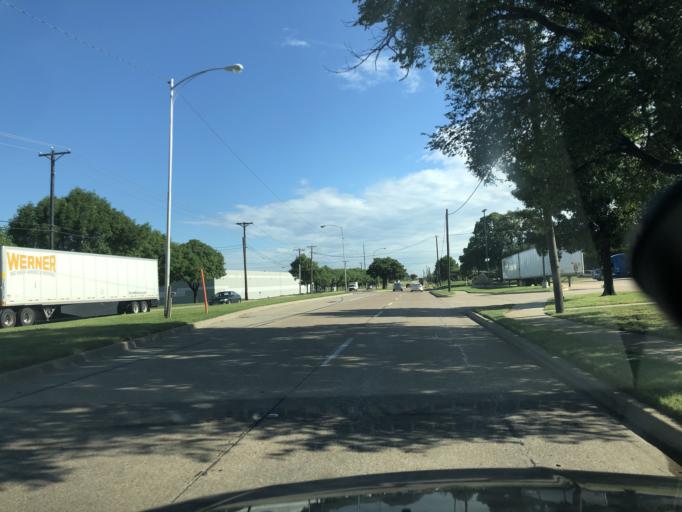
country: US
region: Texas
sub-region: Tarrant County
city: Euless
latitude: 32.8086
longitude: -97.0303
